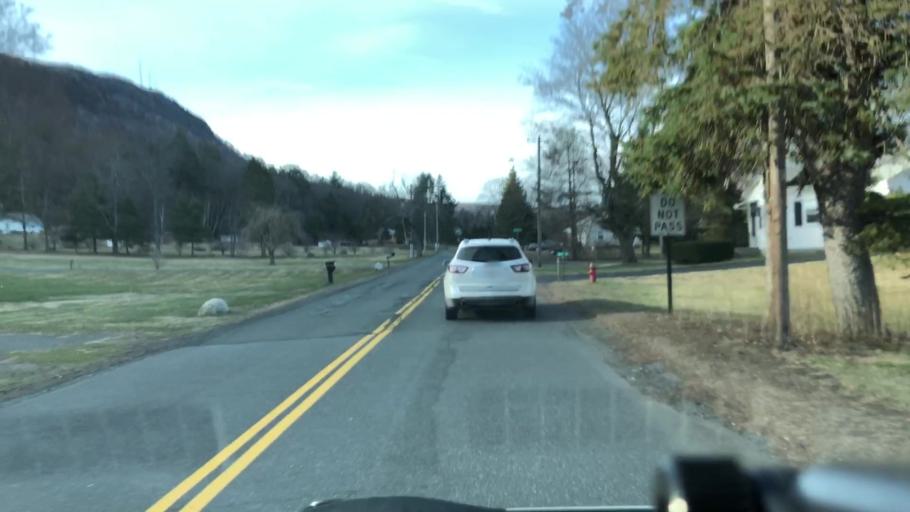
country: US
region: Massachusetts
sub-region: Hampshire County
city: Easthampton
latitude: 42.2551
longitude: -72.6524
